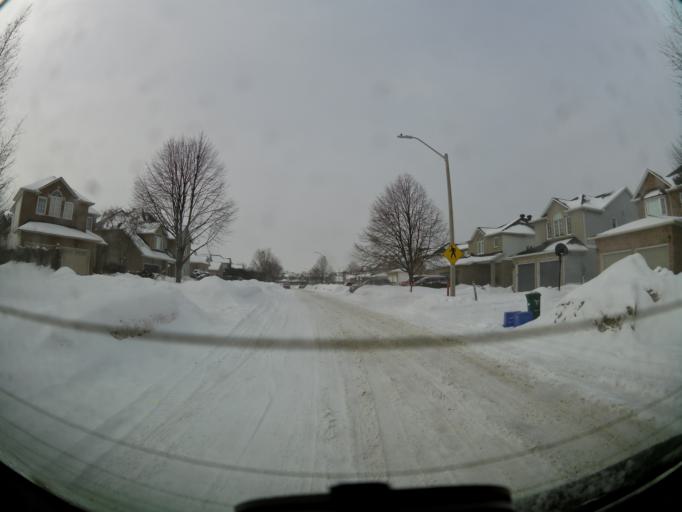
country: CA
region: Ontario
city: Ottawa
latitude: 45.3763
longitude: -75.5995
